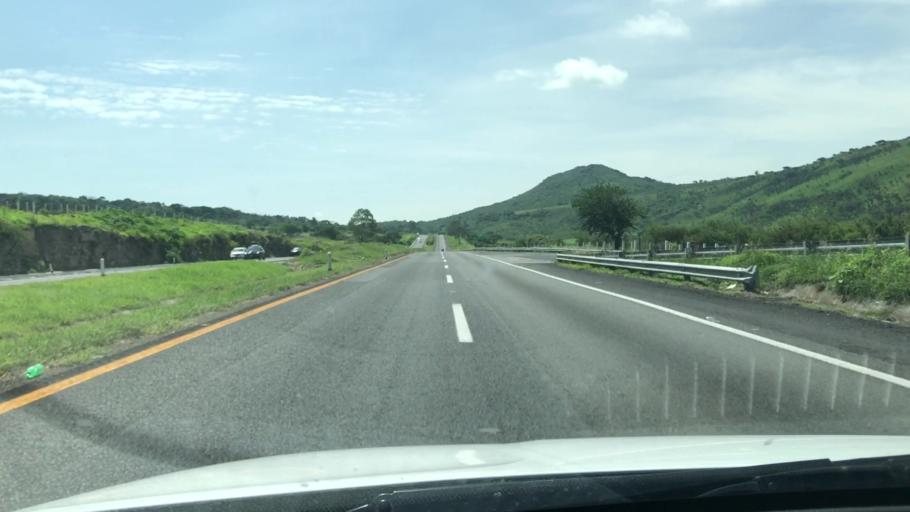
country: MX
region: Jalisco
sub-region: Zapotlan del Rey
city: Zapotlan del Rey
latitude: 20.5254
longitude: -103.0003
